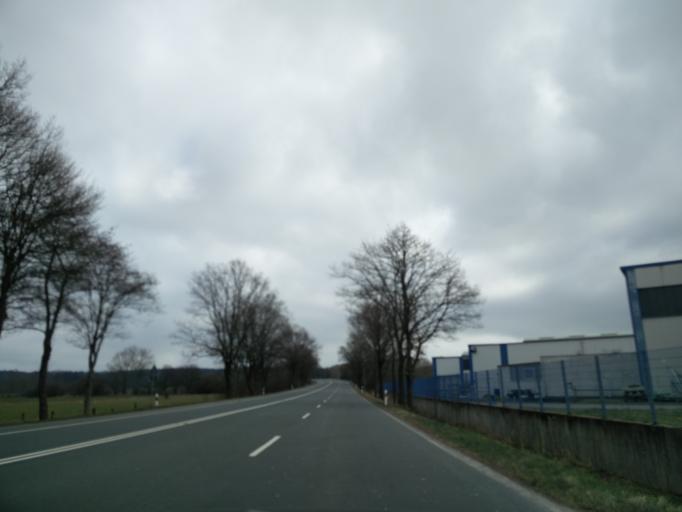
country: DE
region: North Rhine-Westphalia
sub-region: Regierungsbezirk Detmold
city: Willebadessen
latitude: 51.5802
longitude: 8.9844
